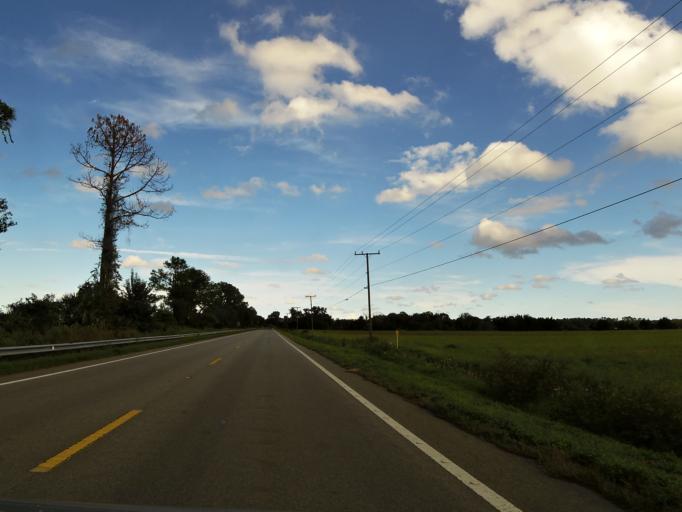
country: US
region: Florida
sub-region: Flagler County
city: Bunnell
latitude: 29.4822
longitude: -81.3605
